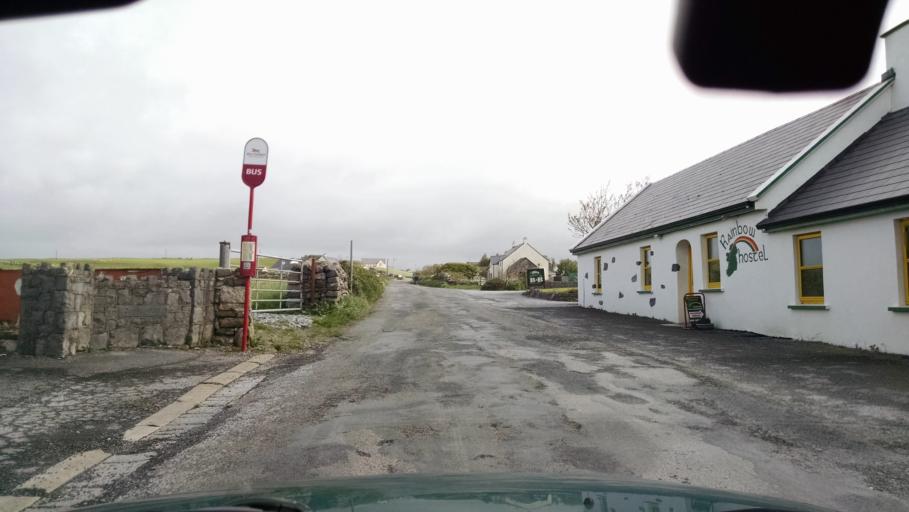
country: IE
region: Connaught
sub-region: County Galway
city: Bearna
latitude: 53.0197
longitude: -9.3709
